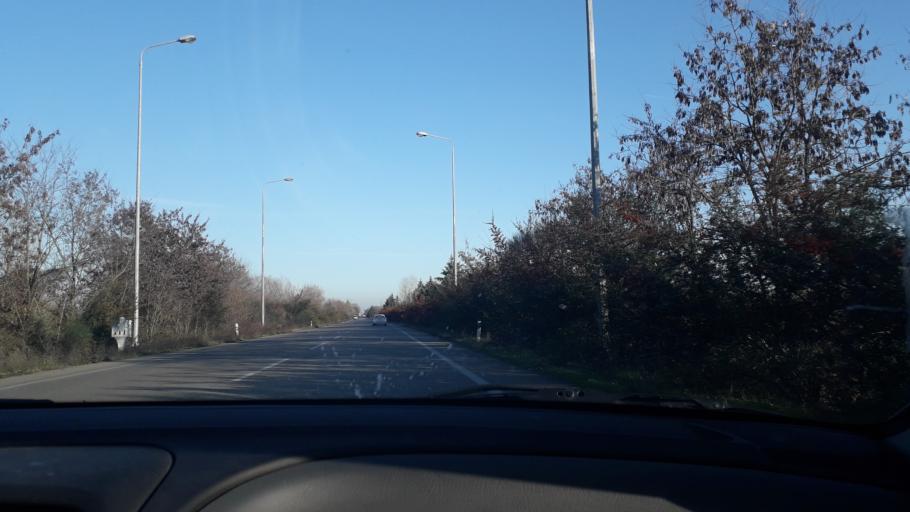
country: GR
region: Central Macedonia
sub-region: Nomos Pellis
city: Karyotissa
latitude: 40.7780
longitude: 22.3222
